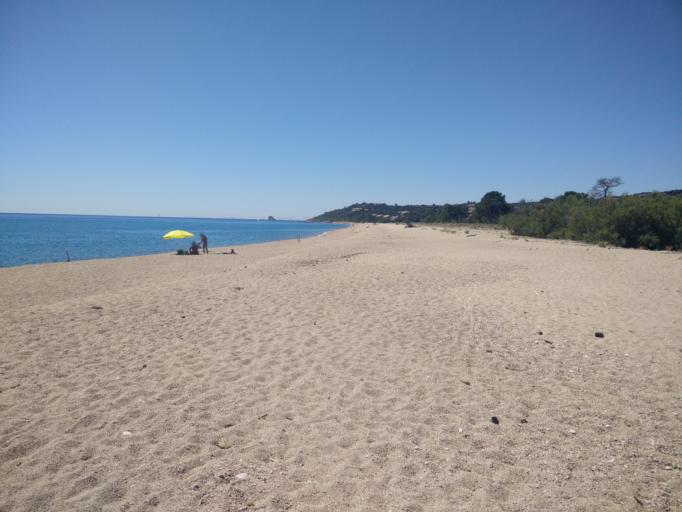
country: FR
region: Corsica
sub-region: Departement de la Corse-du-Sud
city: Sari-Solenzara
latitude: 41.7076
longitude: 9.4017
